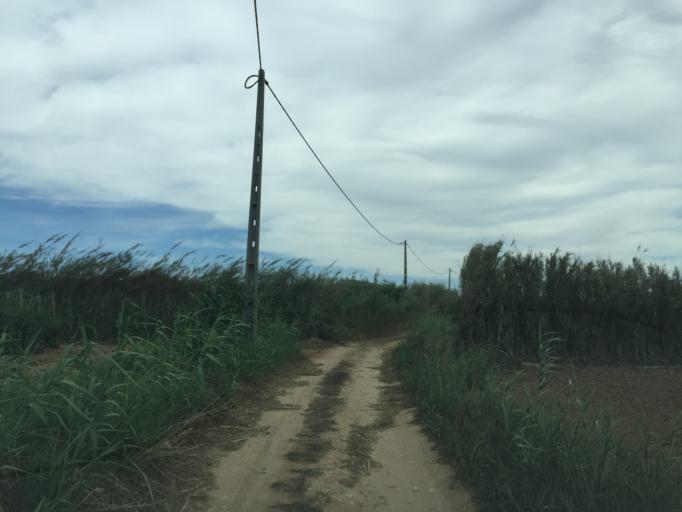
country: PT
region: Lisbon
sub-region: Lourinha
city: Lourinha
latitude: 39.1893
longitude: -9.3446
